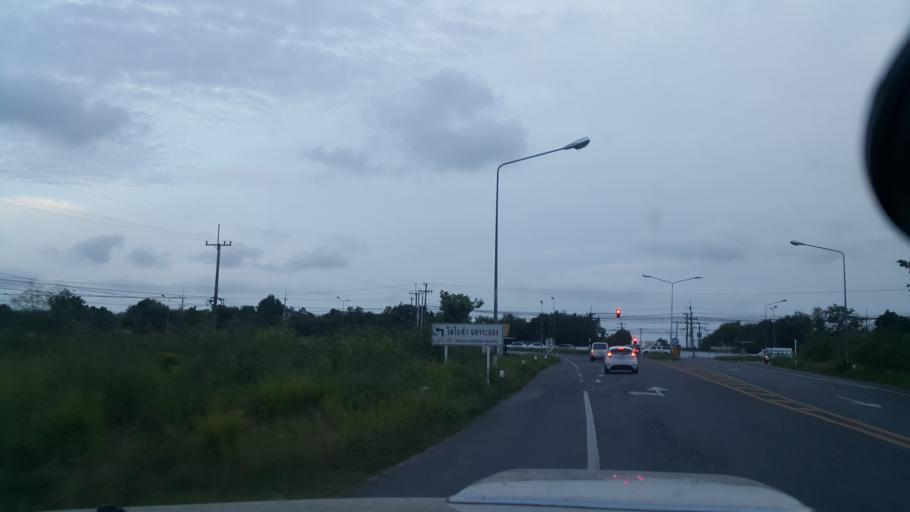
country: TH
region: Rayong
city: Ban Chang
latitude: 12.7039
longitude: 101.0100
